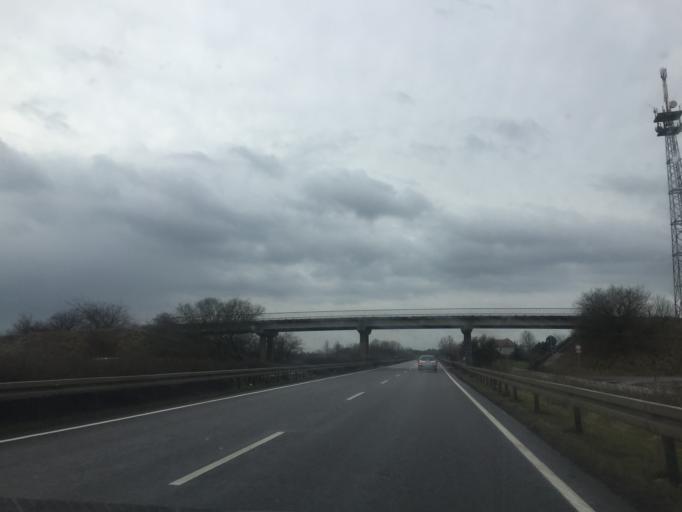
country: DE
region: Saxony-Anhalt
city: Hohendodeleben
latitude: 52.0584
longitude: 11.5433
